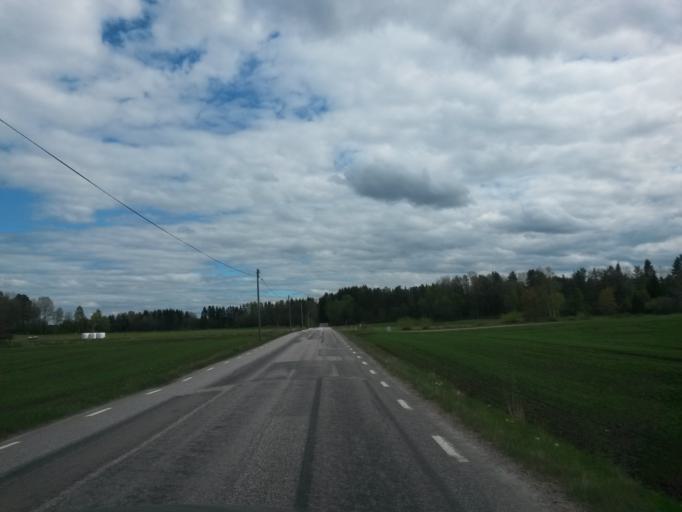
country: SE
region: Vaestra Goetaland
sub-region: Vargarda Kommun
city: Vargarda
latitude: 58.1123
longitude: 12.7975
